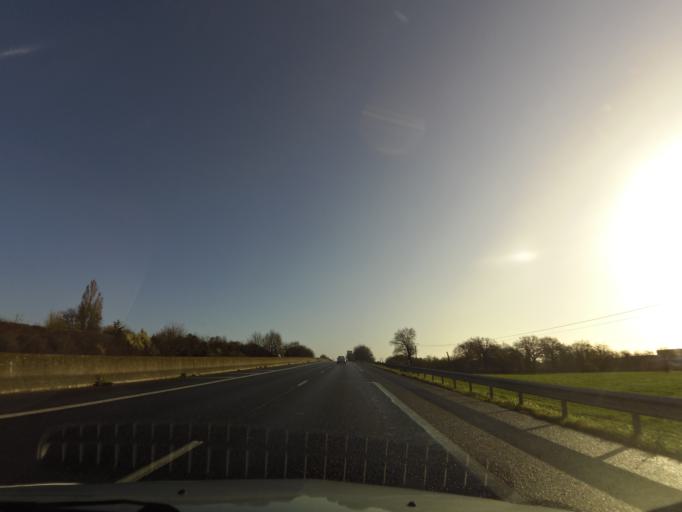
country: FR
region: Brittany
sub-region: Departement d'Ille-et-Vilaine
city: Chantepie
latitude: 48.0888
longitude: -1.6322
